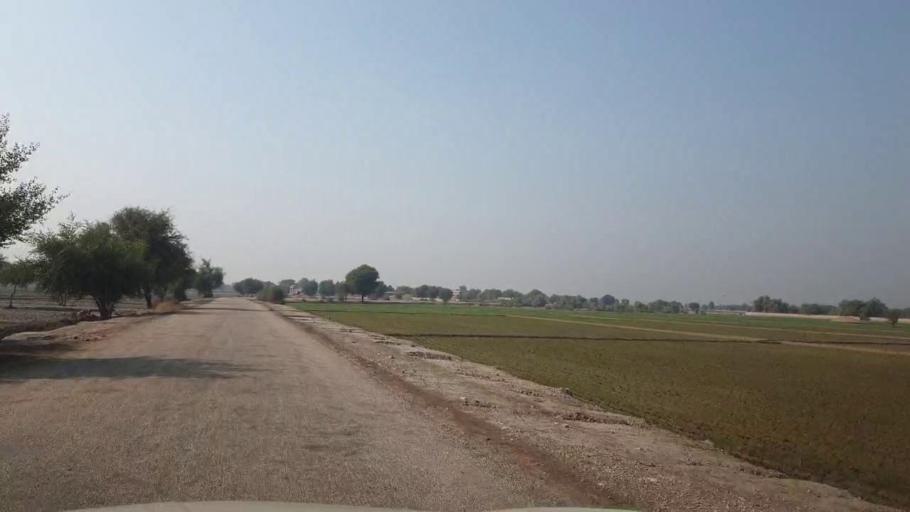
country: PK
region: Sindh
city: Bhan
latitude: 26.5090
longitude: 67.7929
